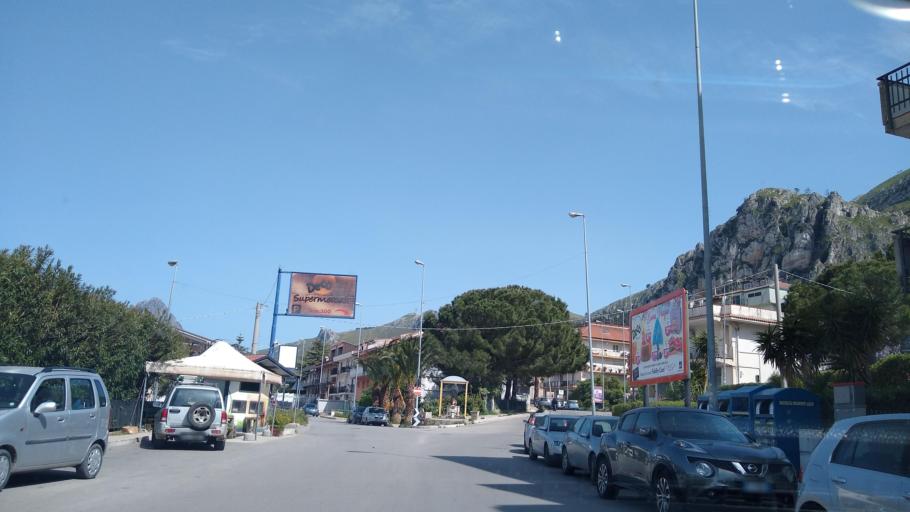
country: IT
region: Sicily
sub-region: Palermo
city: San Giuseppe Jato
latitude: 37.9750
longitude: 13.1936
